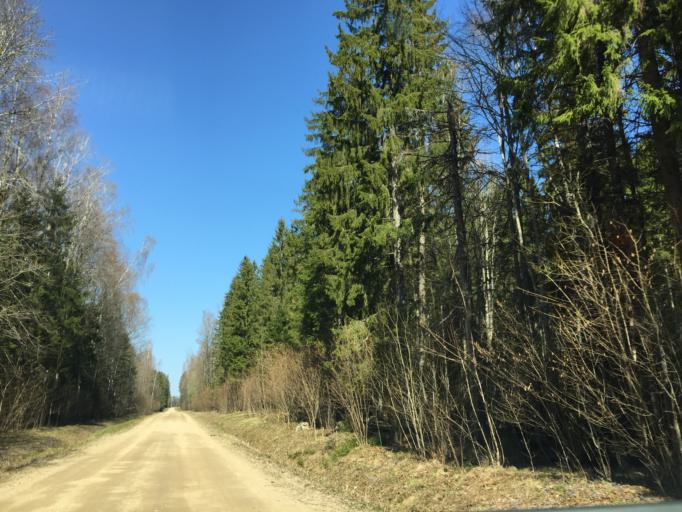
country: EE
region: Tartu
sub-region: Alatskivi vald
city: Kallaste
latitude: 58.5481
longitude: 26.9375
